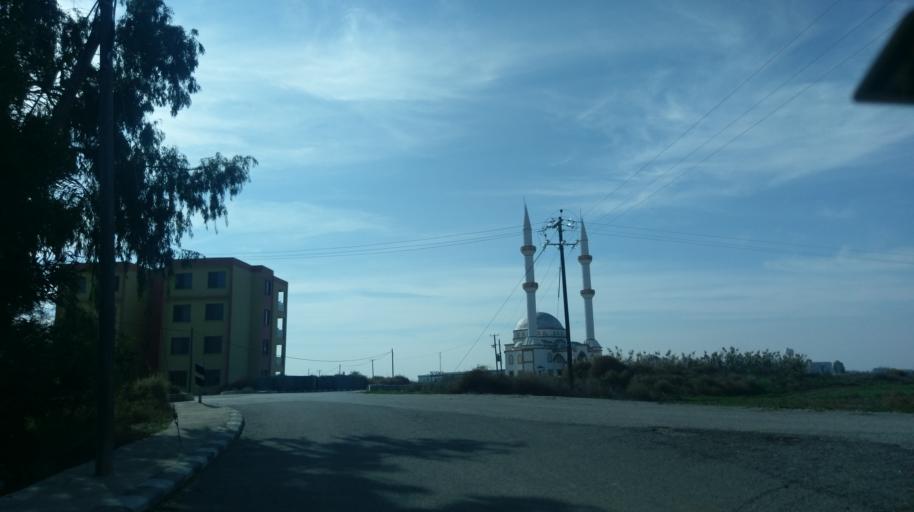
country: CY
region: Ammochostos
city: Lefkonoiko
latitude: 35.1914
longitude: 33.6401
